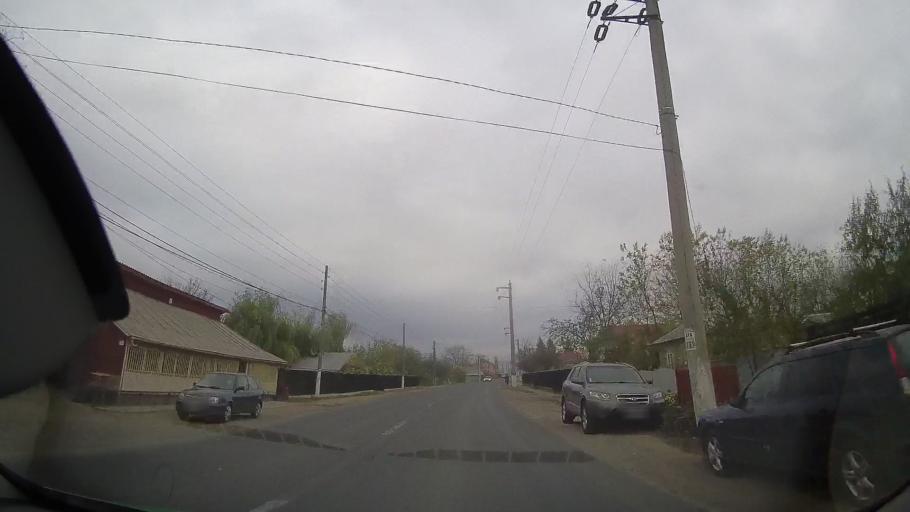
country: RO
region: Buzau
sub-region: Comuna Padina
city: Padina
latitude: 44.8235
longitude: 27.1137
